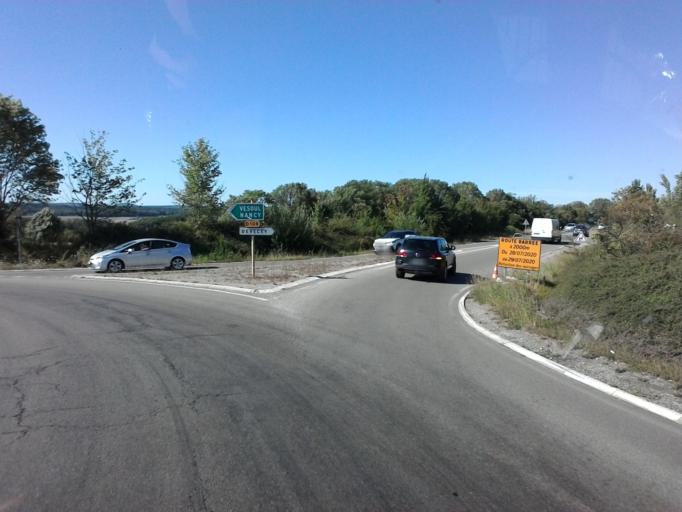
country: FR
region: Franche-Comte
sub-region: Departement du Doubs
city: Chatillon-le-Duc
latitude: 47.3193
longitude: 5.9995
